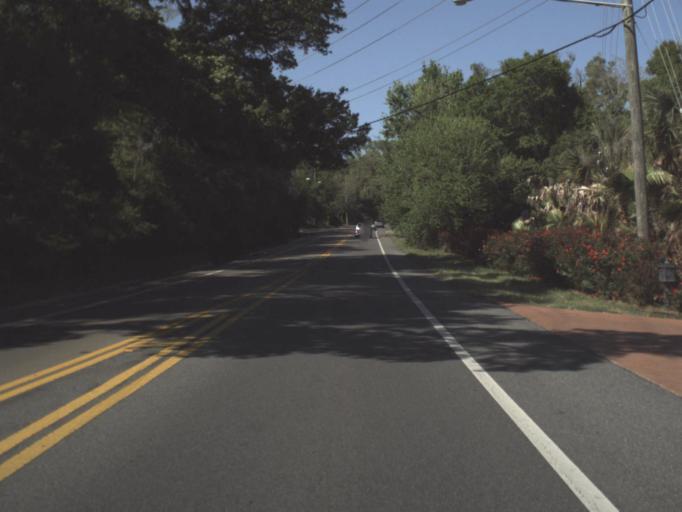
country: US
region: Florida
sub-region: Escambia County
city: East Pensacola Heights
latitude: 30.4826
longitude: -87.1619
